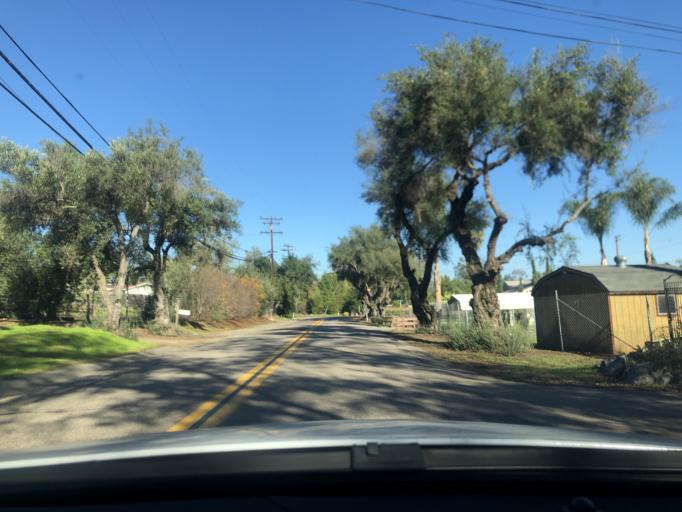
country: US
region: California
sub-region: San Diego County
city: Rancho San Diego
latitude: 32.7705
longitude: -116.9387
